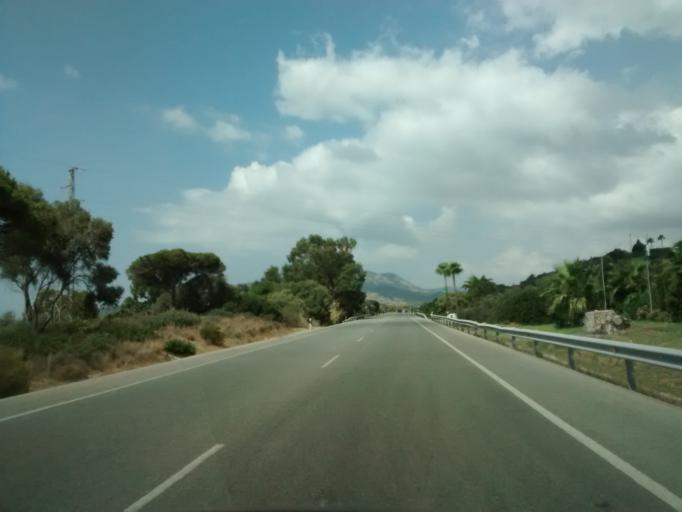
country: ES
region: Andalusia
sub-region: Provincia de Cadiz
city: Tarifa
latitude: 36.0593
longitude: -5.6671
